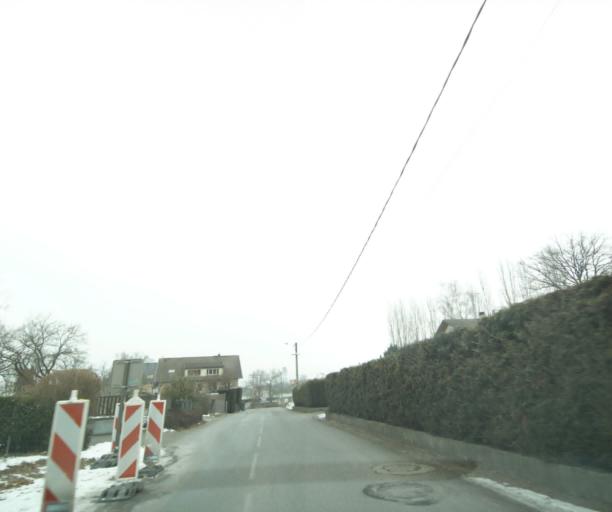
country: FR
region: Rhone-Alpes
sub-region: Departement de la Haute-Savoie
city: Reignier-Esery
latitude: 46.1312
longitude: 6.2963
